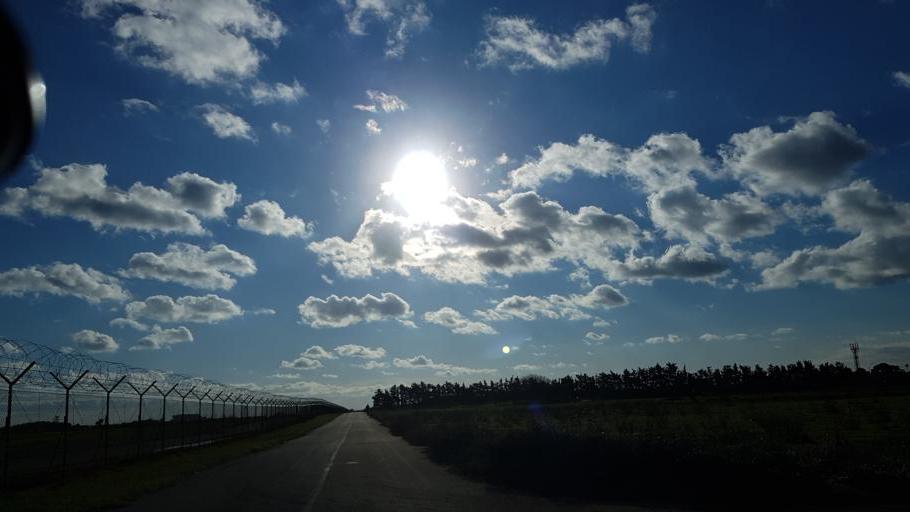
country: IT
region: Apulia
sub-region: Provincia di Brindisi
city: Materdomini
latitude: 40.6698
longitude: 17.9301
